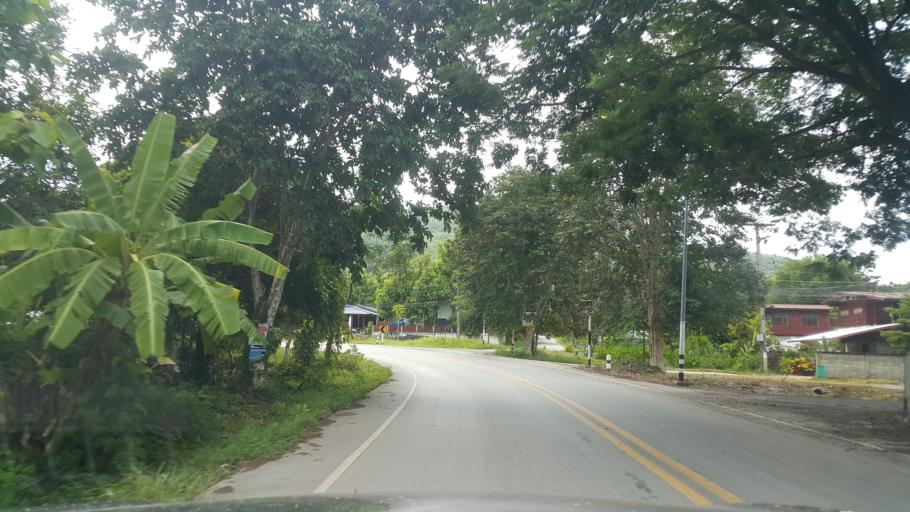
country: TH
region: Uttaradit
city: Thong Saen Khan
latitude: 17.4098
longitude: 100.3227
